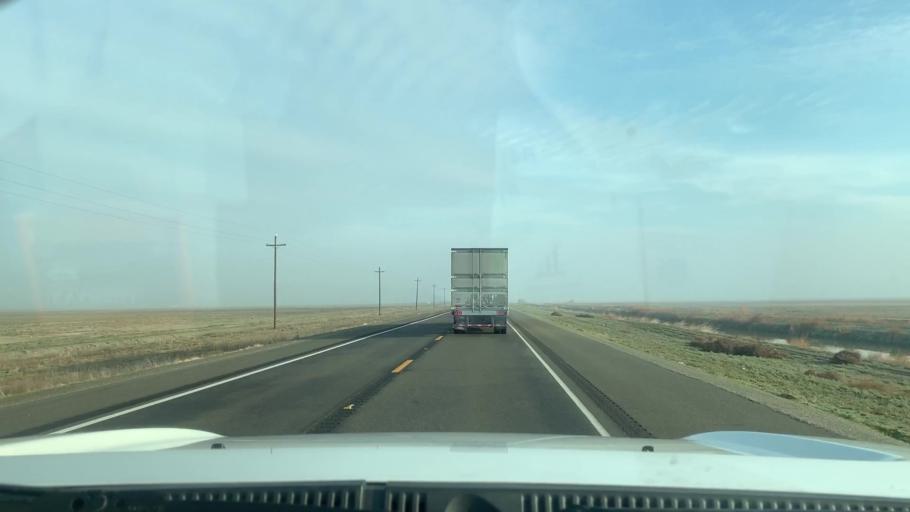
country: US
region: California
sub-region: Kings County
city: Kettleman City
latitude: 36.0816
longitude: -119.9196
